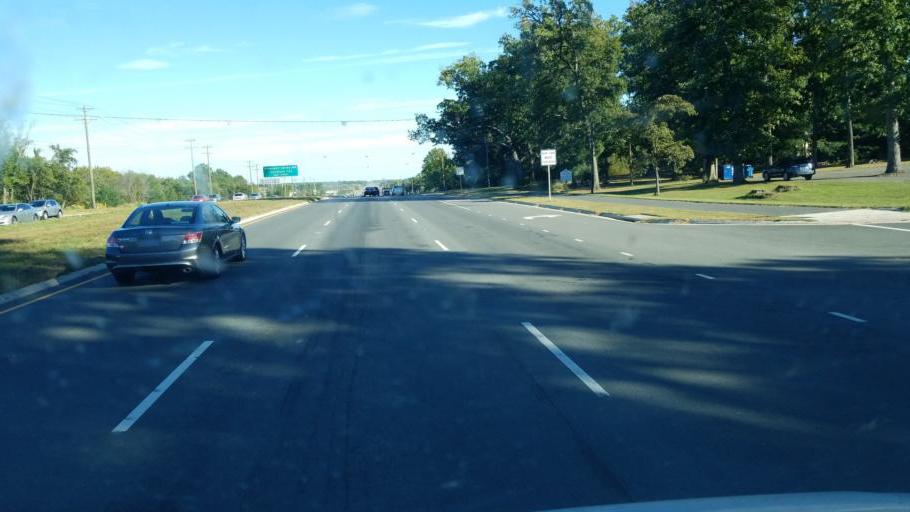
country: US
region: Virginia
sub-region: Loudoun County
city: South Riding
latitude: 38.9143
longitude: -77.4812
